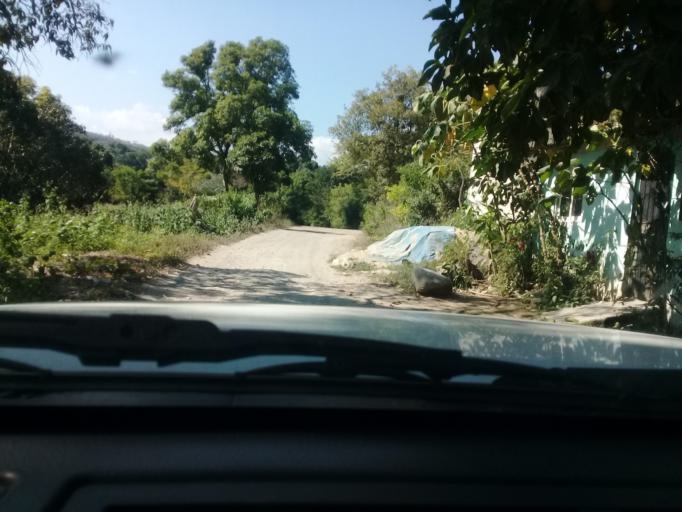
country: MX
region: Veracruz
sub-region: Emiliano Zapata
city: Plan del Rio
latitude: 19.4267
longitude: -96.6158
